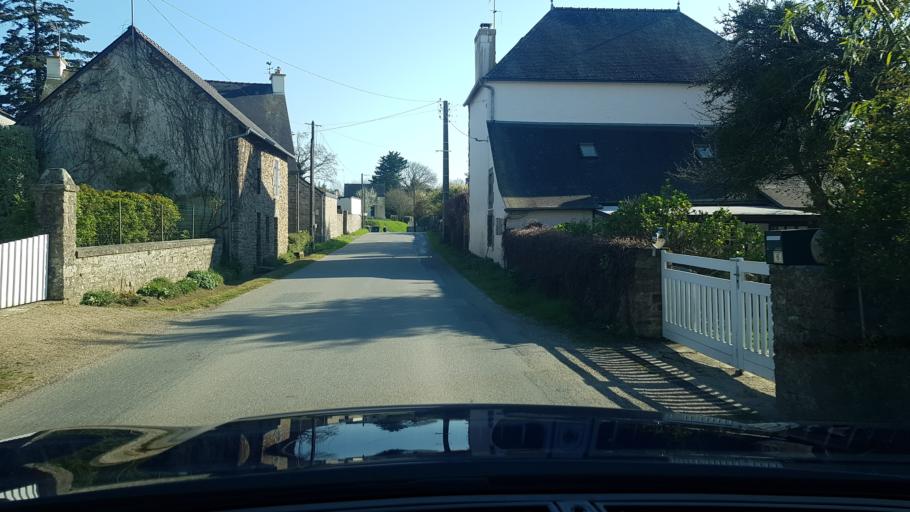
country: FR
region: Brittany
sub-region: Departement du Finistere
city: Moelan-sur-Mer
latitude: 47.7992
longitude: -3.6247
